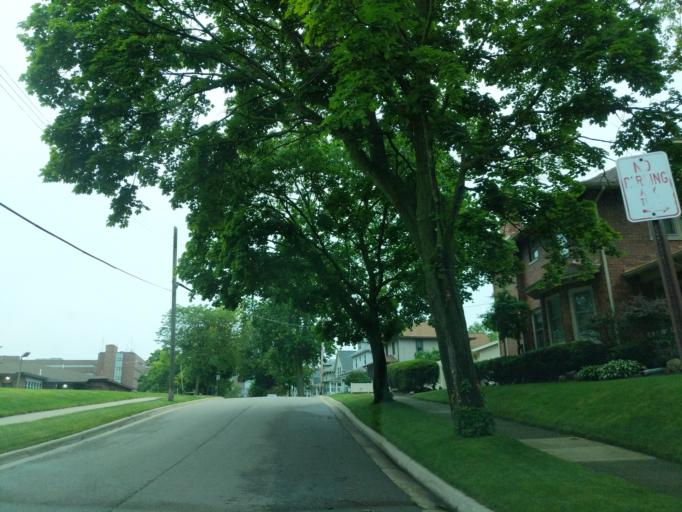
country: US
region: Michigan
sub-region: Jackson County
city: Jackson
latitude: 42.2519
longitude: -84.3892
